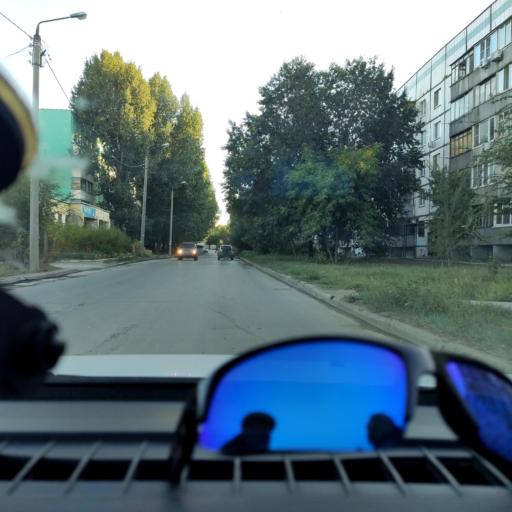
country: RU
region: Samara
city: Samara
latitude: 53.1222
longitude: 50.0952
